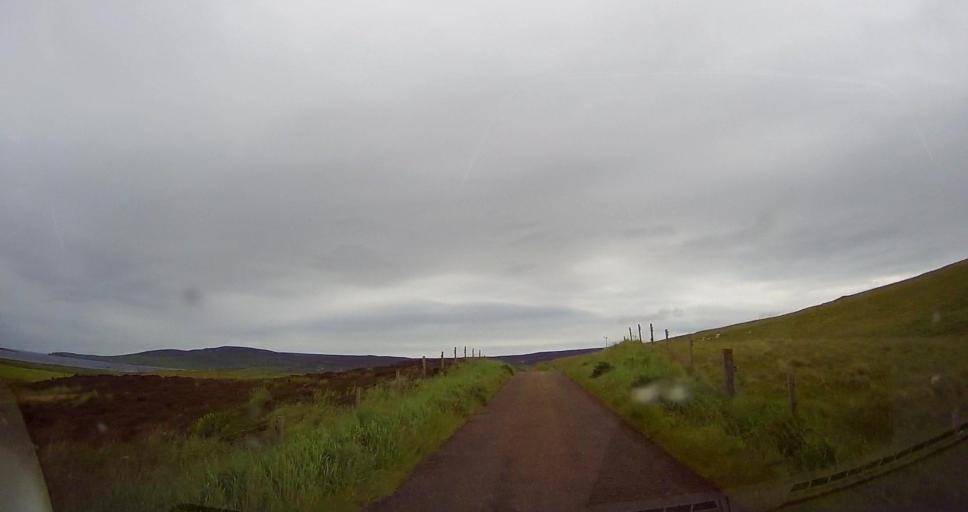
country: GB
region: Scotland
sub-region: Orkney Islands
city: Orkney
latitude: 59.1072
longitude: -3.0833
